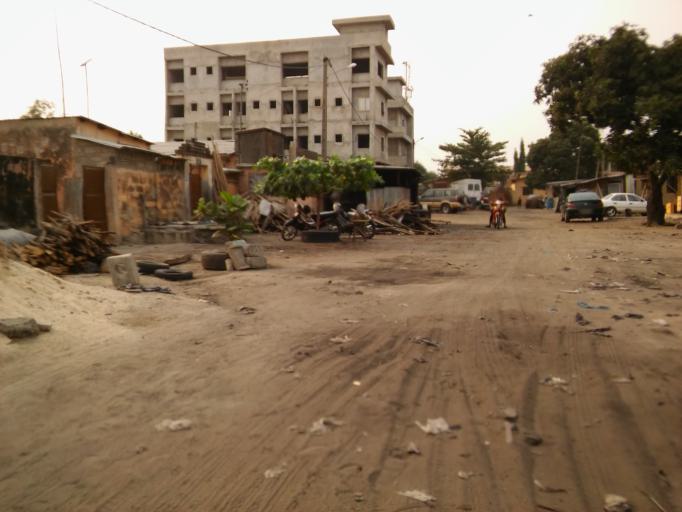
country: BJ
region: Littoral
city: Cotonou
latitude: 6.3585
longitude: 2.4074
